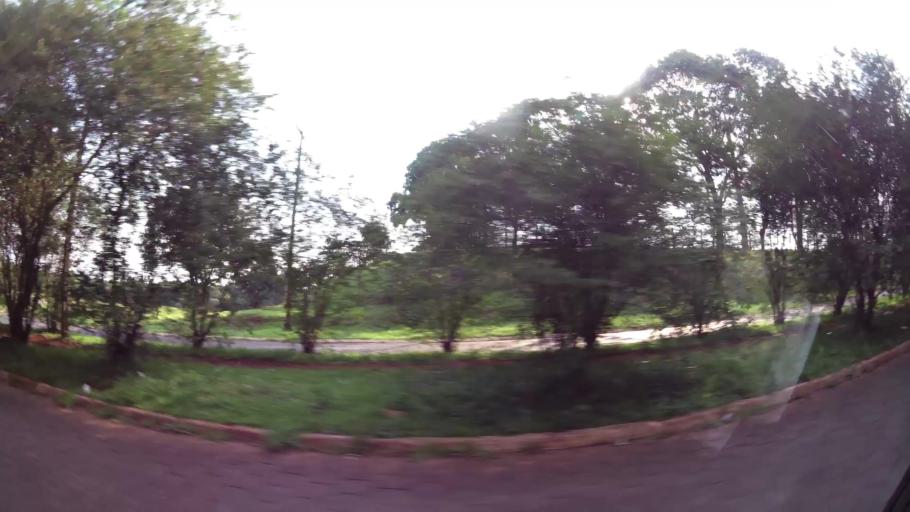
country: PY
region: Alto Parana
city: Presidente Franco
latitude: -25.5231
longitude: -54.6358
